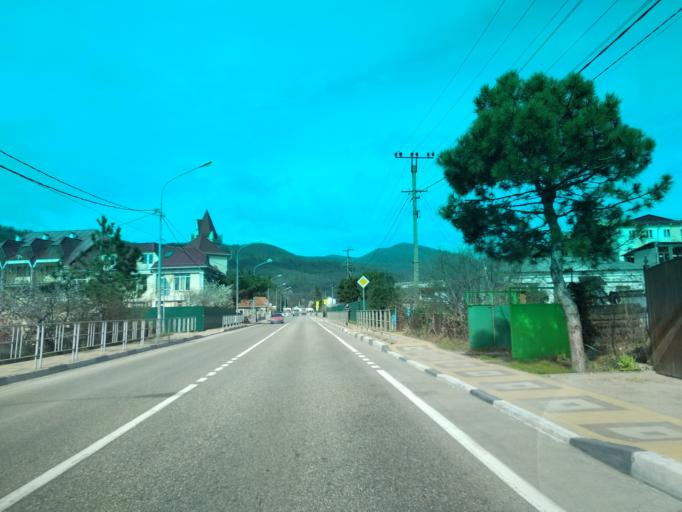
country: RU
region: Krasnodarskiy
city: Shepsi
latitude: 44.0383
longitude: 39.1506
